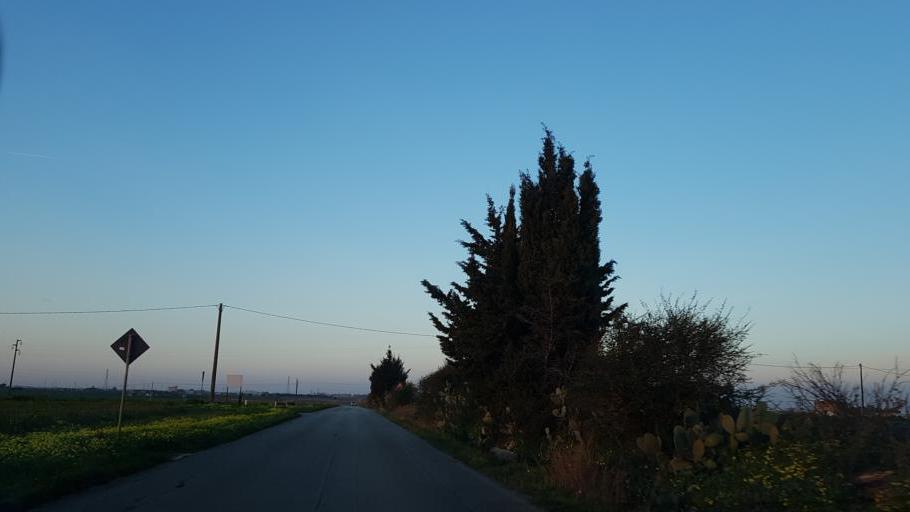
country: IT
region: Apulia
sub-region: Provincia di Brindisi
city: Tuturano
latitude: 40.5745
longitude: 17.9496
